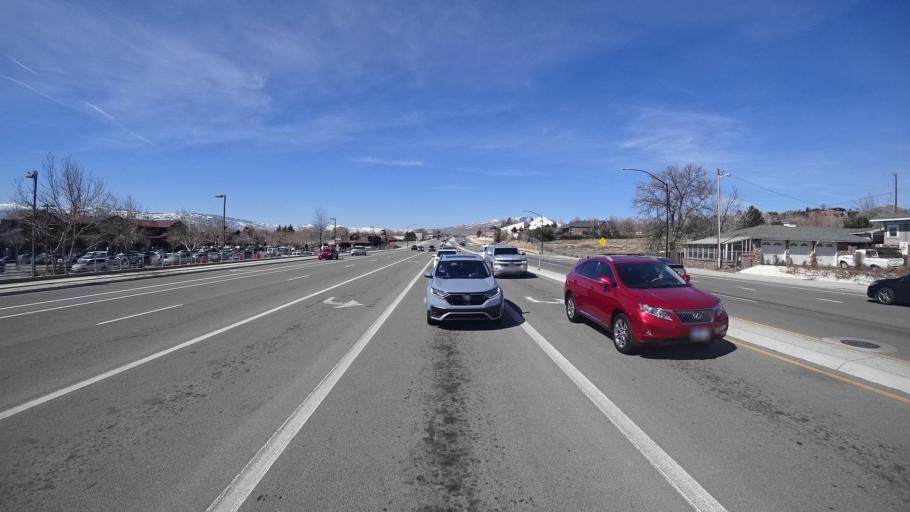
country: US
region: Nevada
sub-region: Washoe County
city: Sparks
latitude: 39.5559
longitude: -119.7528
